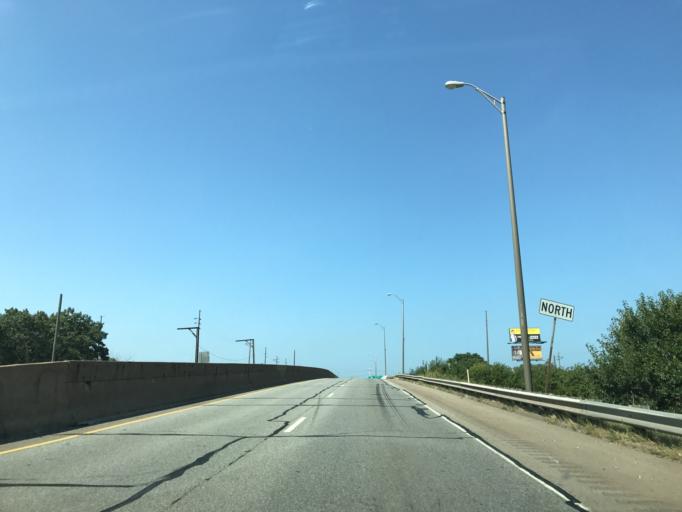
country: US
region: Indiana
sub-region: Lake County
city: East Chicago
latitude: 41.6082
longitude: -87.4325
